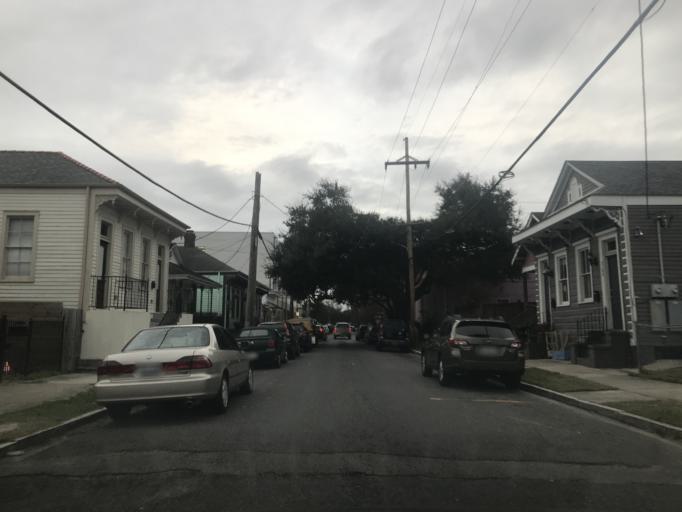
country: US
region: Louisiana
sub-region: Orleans Parish
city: New Orleans
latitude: 29.9673
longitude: -90.0922
